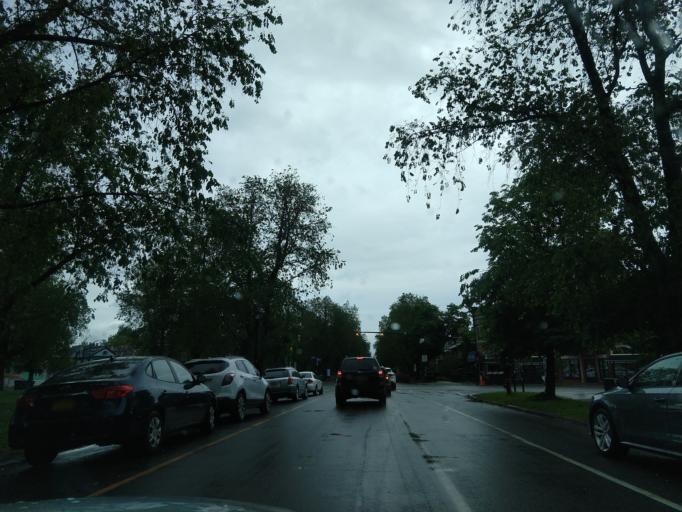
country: US
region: New York
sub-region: Erie County
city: Buffalo
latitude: 42.9229
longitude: -78.8775
